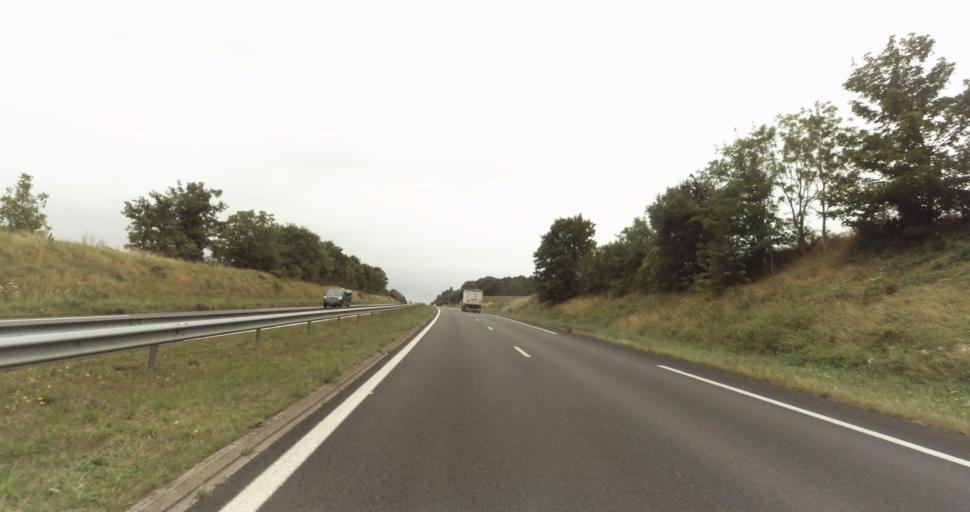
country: FR
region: Haute-Normandie
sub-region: Departement de l'Eure
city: Acquigny
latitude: 49.1697
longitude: 1.1713
